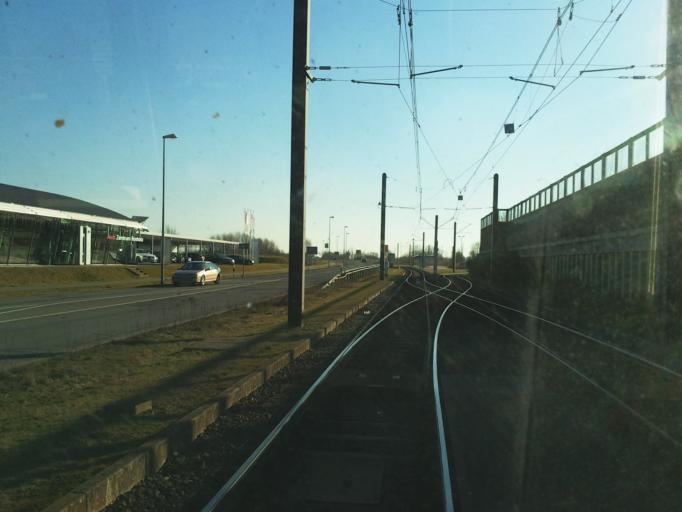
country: DE
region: Mecklenburg-Vorpommern
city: Papendorf
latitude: 54.0593
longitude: 12.1171
